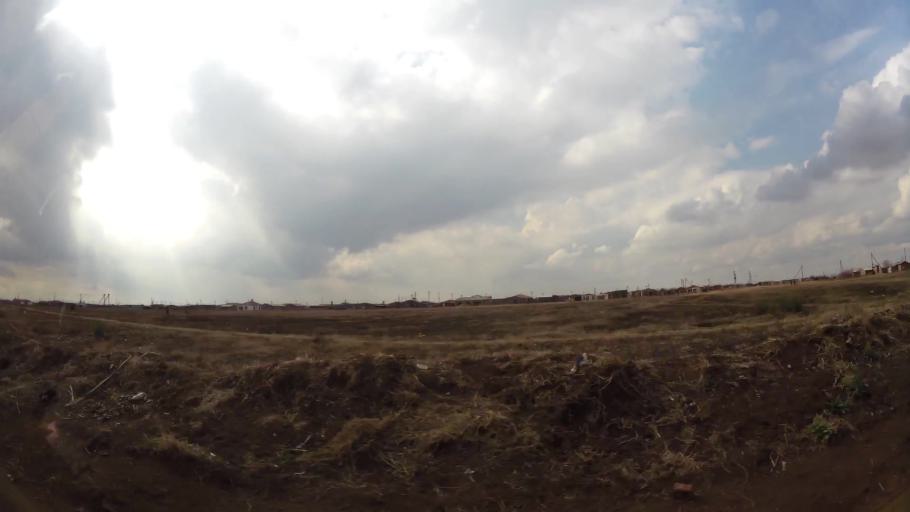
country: ZA
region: Orange Free State
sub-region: Fezile Dabi District Municipality
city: Sasolburg
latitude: -26.8569
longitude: 27.8993
